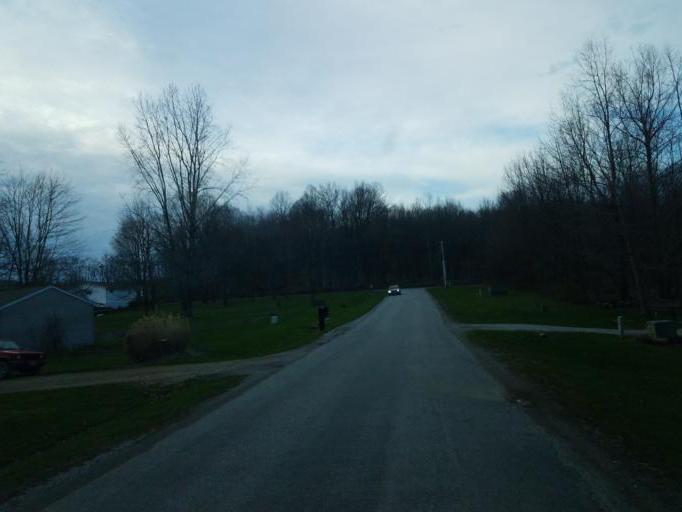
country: US
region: Ohio
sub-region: Knox County
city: Danville
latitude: 40.4670
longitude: -82.3449
